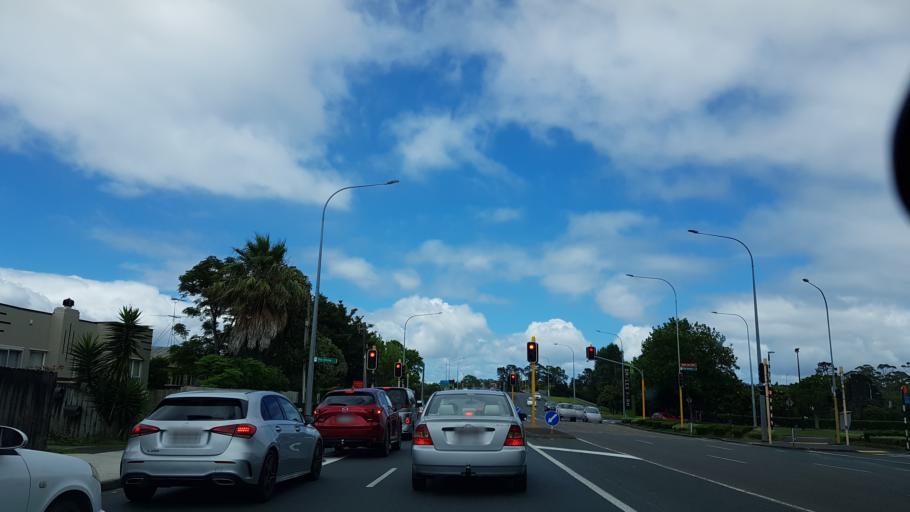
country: NZ
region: Auckland
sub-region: Auckland
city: North Shore
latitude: -36.7862
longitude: 174.7554
